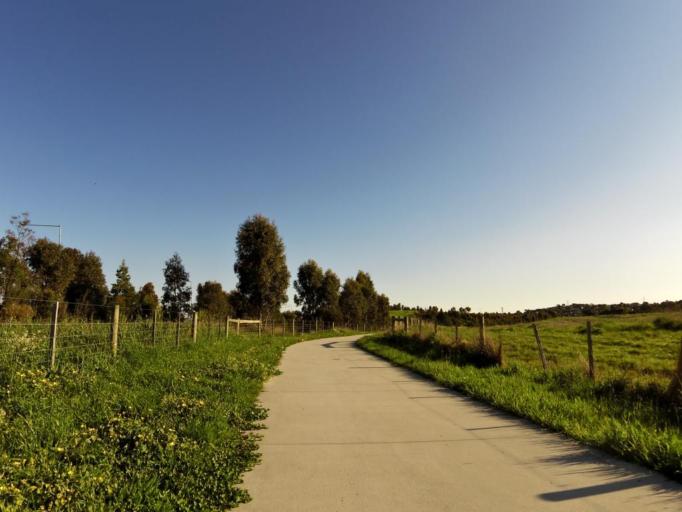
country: AU
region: Victoria
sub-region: Monash
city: Mulgrave
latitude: -37.9220
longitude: 145.2137
